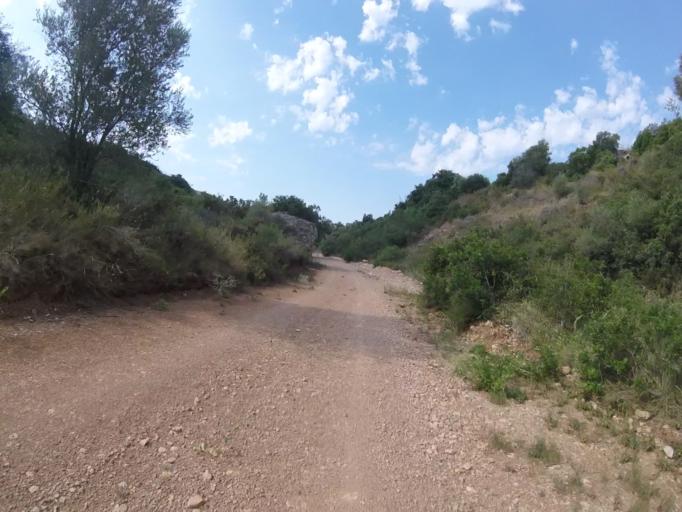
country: ES
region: Valencia
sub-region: Provincia de Castello
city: Alcala de Xivert
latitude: 40.3325
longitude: 0.1936
